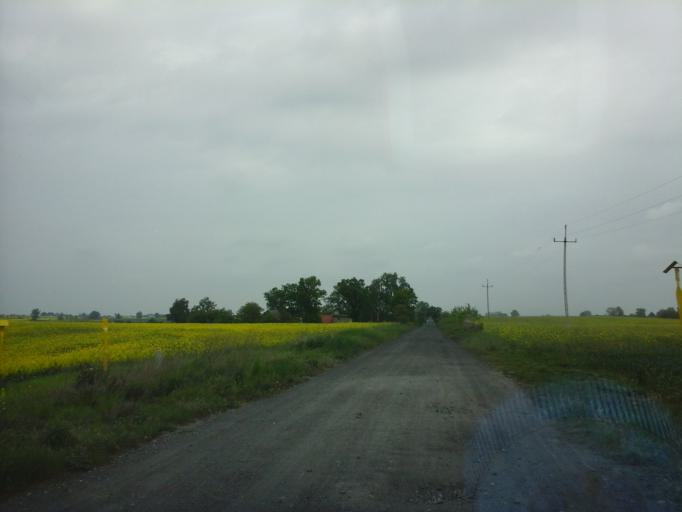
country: PL
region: West Pomeranian Voivodeship
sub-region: Powiat choszczenski
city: Pelczyce
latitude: 53.0095
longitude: 15.3700
